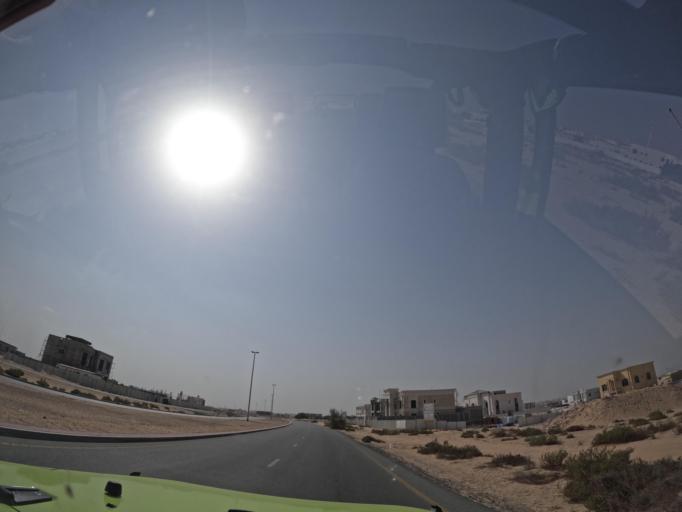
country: AE
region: Ash Shariqah
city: Sharjah
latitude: 25.1959
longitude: 55.4302
